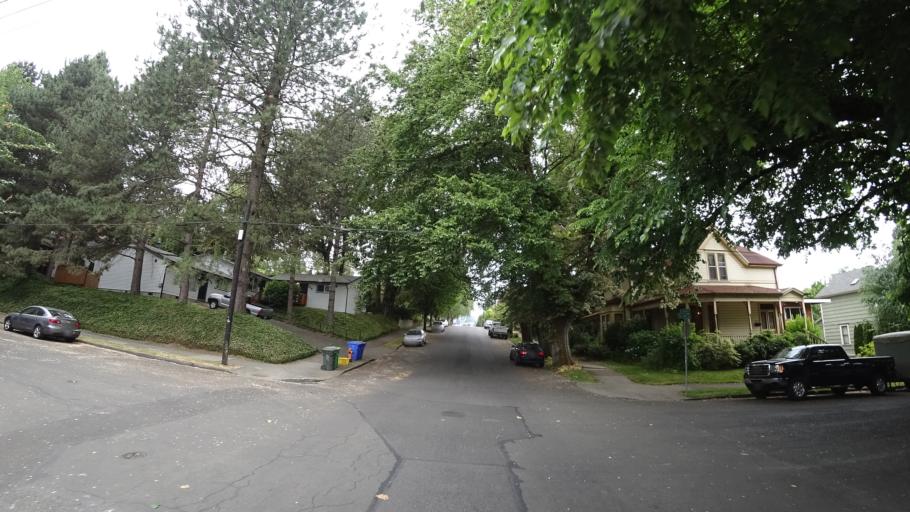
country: US
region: Oregon
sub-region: Multnomah County
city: Portland
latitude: 45.4997
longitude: -122.6567
